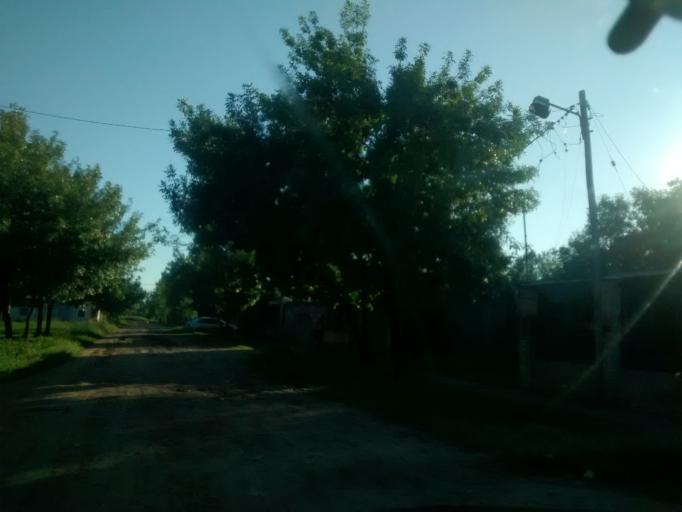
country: AR
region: Chaco
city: Fontana
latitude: -27.4083
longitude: -58.9969
